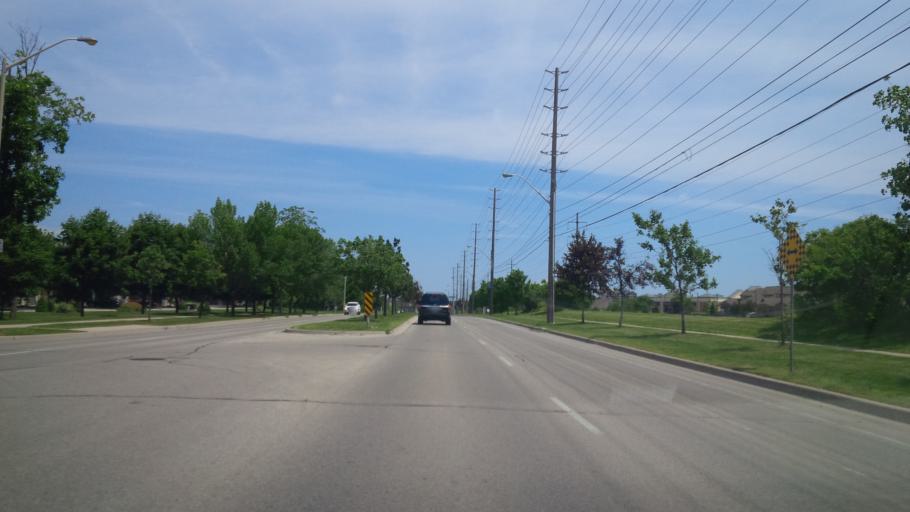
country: CA
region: Ontario
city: Burlington
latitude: 43.3863
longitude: -79.7984
